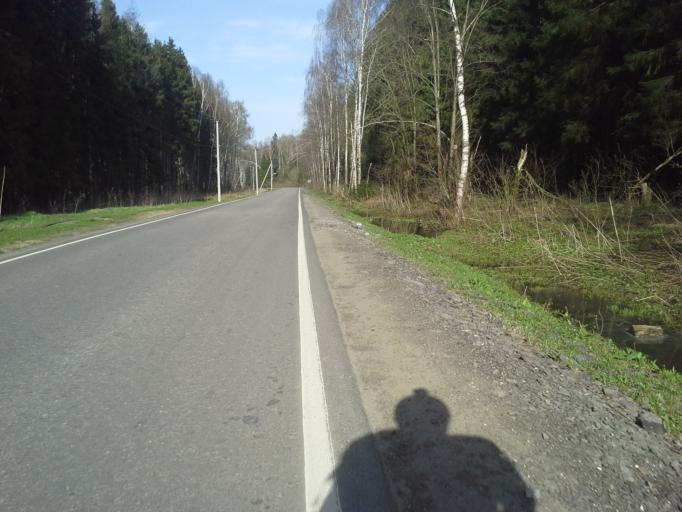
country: RU
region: Moskovskaya
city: Vatutinki
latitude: 55.4703
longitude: 37.3830
